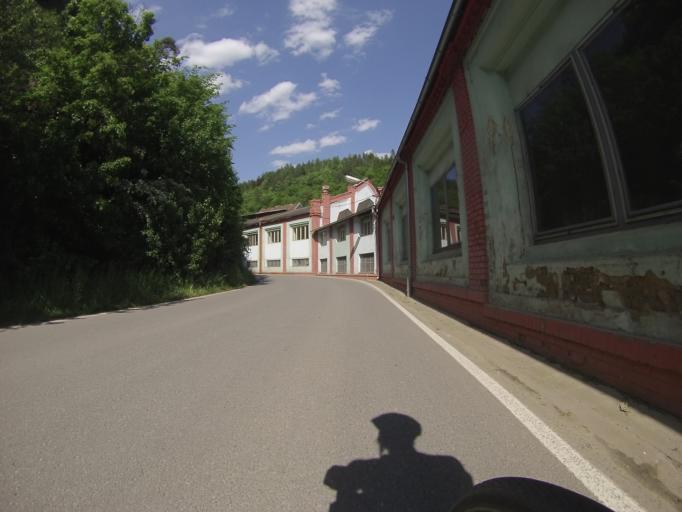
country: CZ
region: South Moravian
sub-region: Okres Blansko
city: Blansko
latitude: 49.3527
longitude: 16.6841
